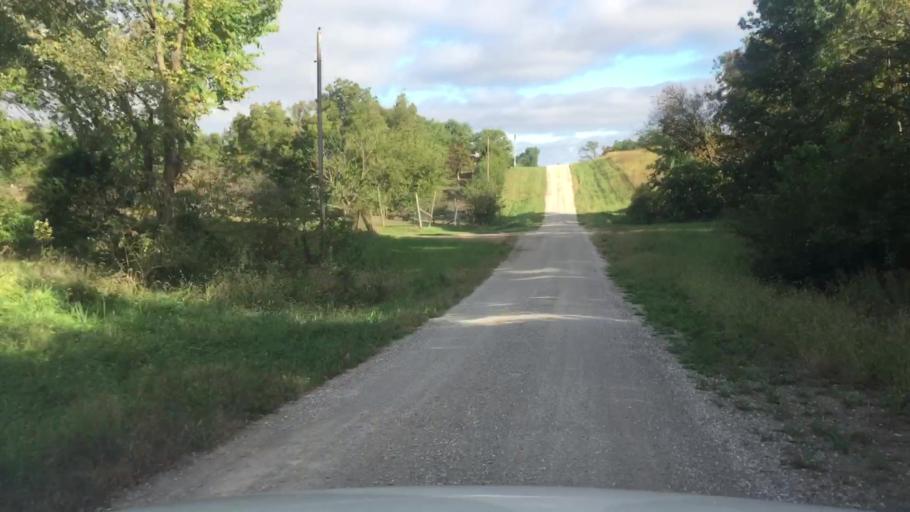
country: US
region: Missouri
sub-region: Howard County
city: New Franklin
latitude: 39.0944
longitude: -92.7796
